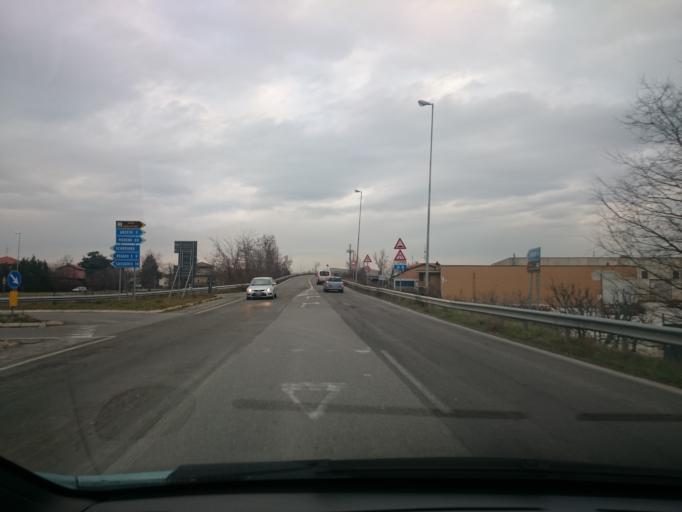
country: IT
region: Emilia-Romagna
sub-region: Provincia di Reggio Emilia
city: Scandiano
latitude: 44.5961
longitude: 10.7034
